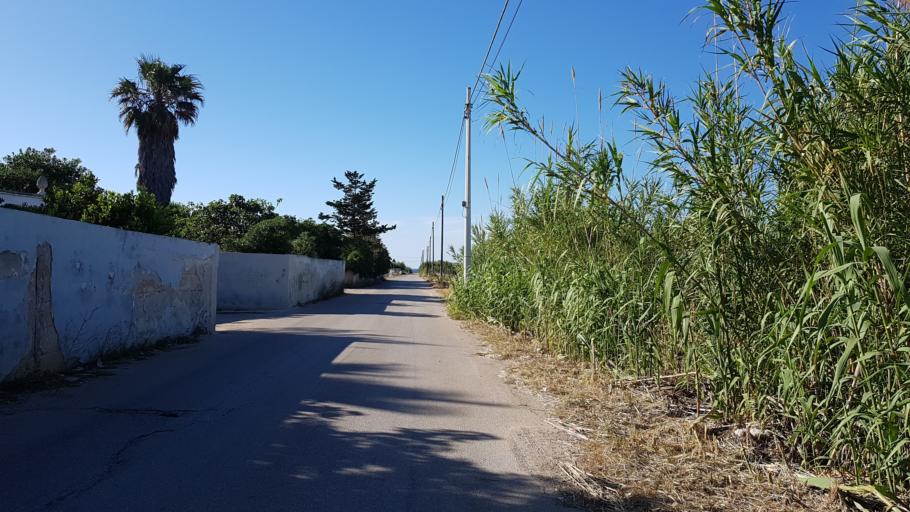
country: IT
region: Apulia
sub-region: Provincia di Brindisi
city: Brindisi
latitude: 40.6816
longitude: 17.8756
